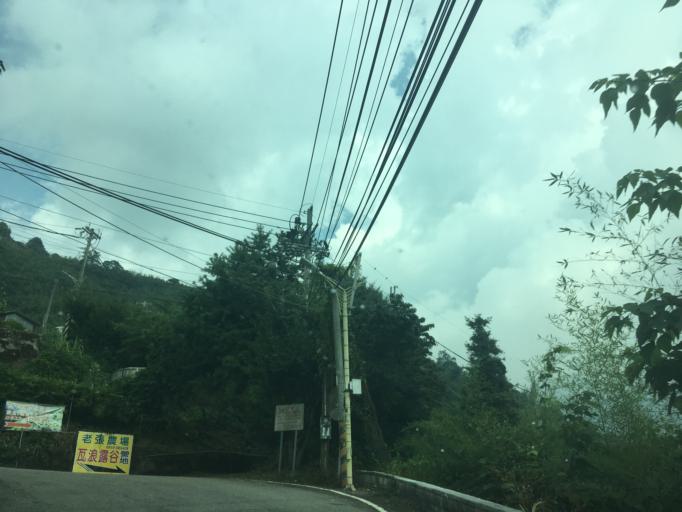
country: TW
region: Taiwan
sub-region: Miaoli
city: Miaoli
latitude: 24.3925
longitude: 120.9791
